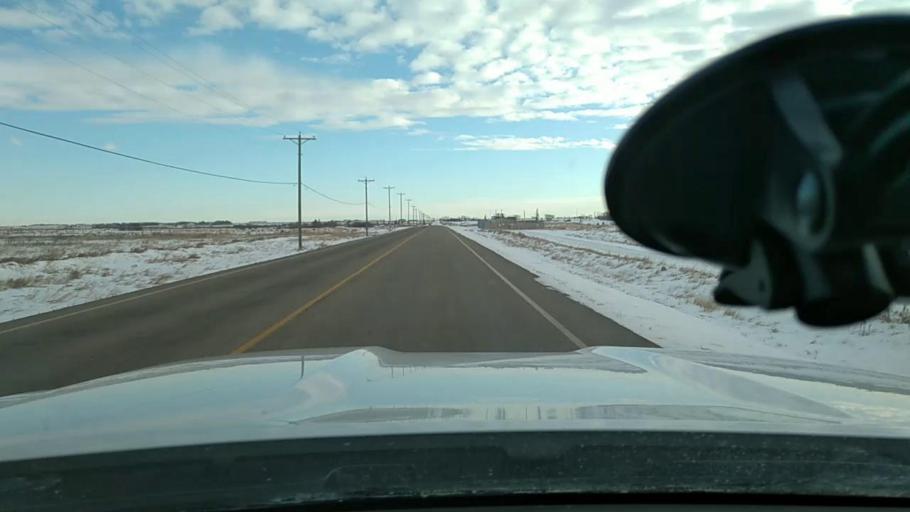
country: CA
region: Alberta
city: Chestermere
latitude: 50.9652
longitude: -113.6707
